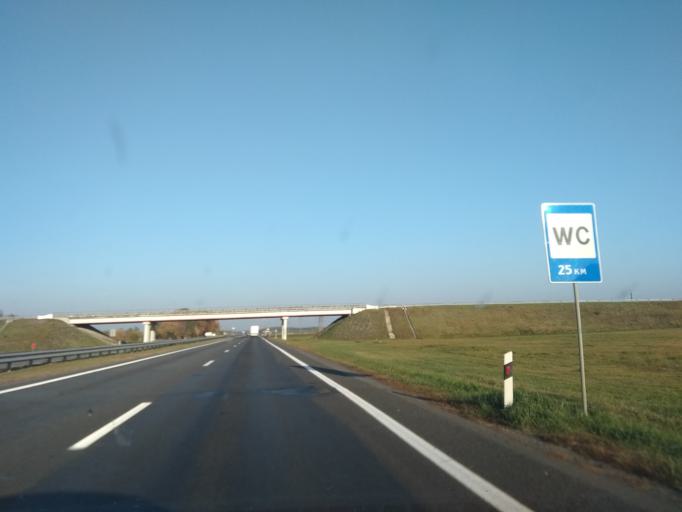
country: BY
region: Brest
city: Zhabinka
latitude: 52.1255
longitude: 23.8971
